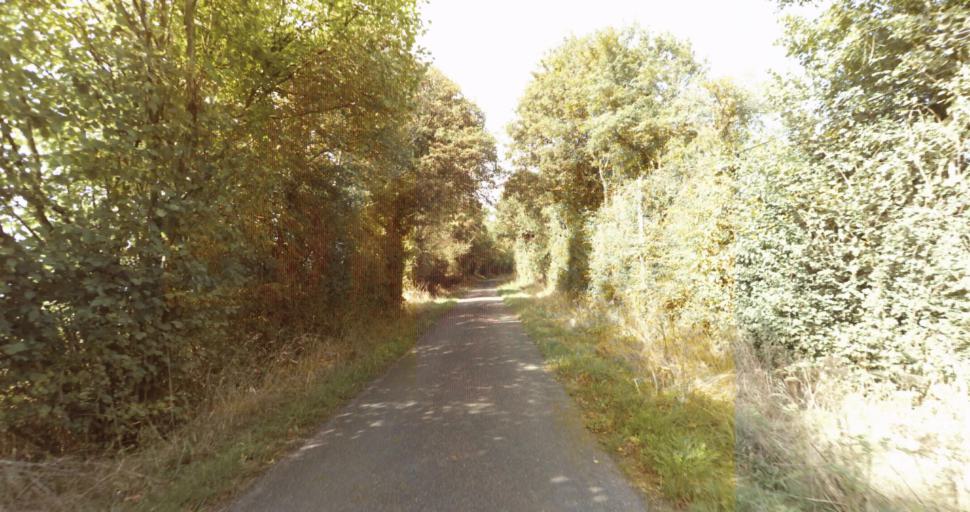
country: FR
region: Lower Normandy
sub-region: Departement de l'Orne
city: Sees
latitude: 48.7097
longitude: 0.1761
